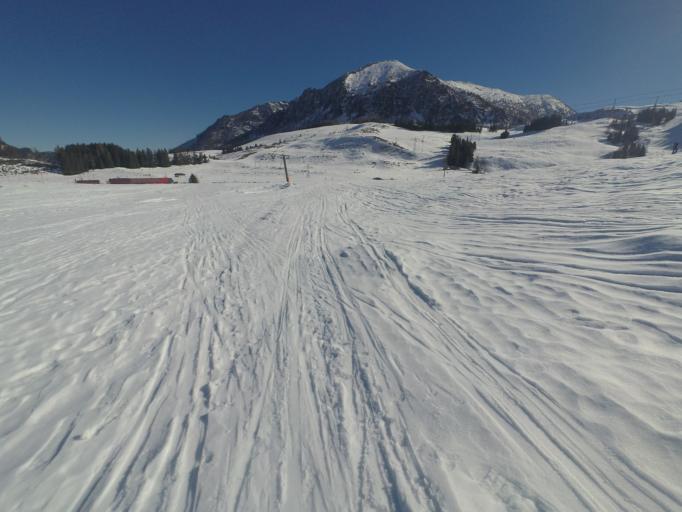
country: AT
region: Salzburg
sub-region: Politischer Bezirk Salzburg-Umgebung
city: Strobl
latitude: 47.6484
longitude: 13.4275
